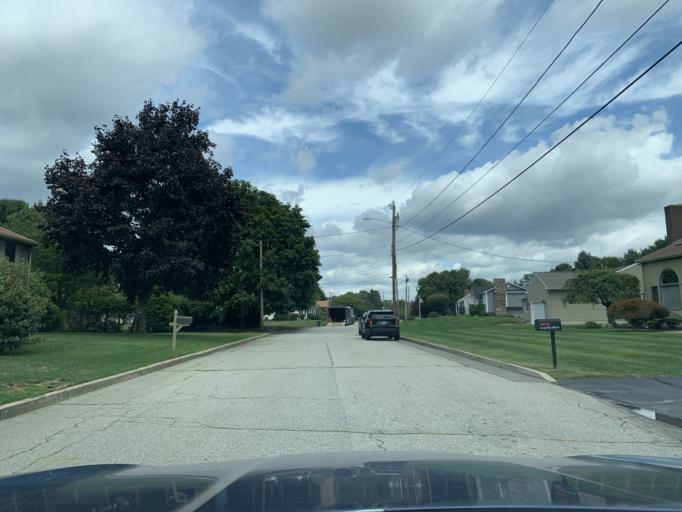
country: US
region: Rhode Island
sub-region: Providence County
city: Johnston
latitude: 41.7791
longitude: -71.4950
